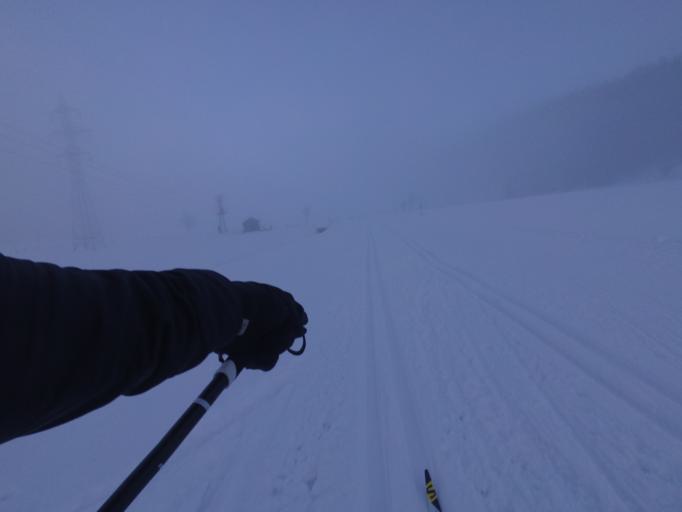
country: AT
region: Salzburg
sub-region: Politischer Bezirk Sankt Johann im Pongau
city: Flachau
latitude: 47.3578
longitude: 13.3509
